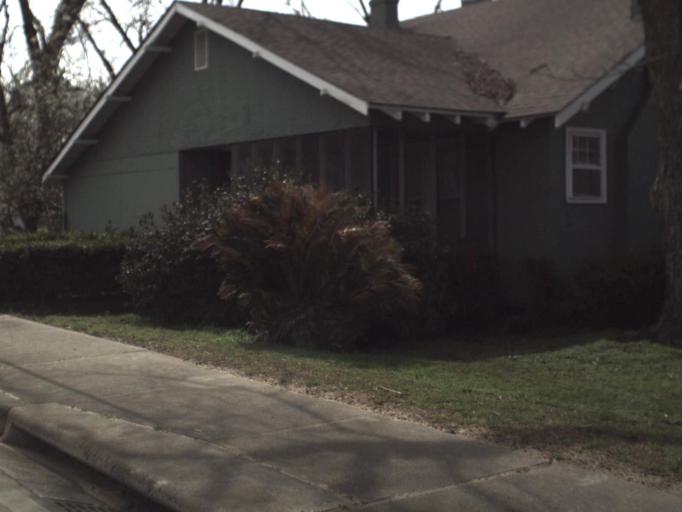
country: US
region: Florida
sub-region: Jackson County
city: Marianna
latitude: 30.7939
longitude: -85.3768
